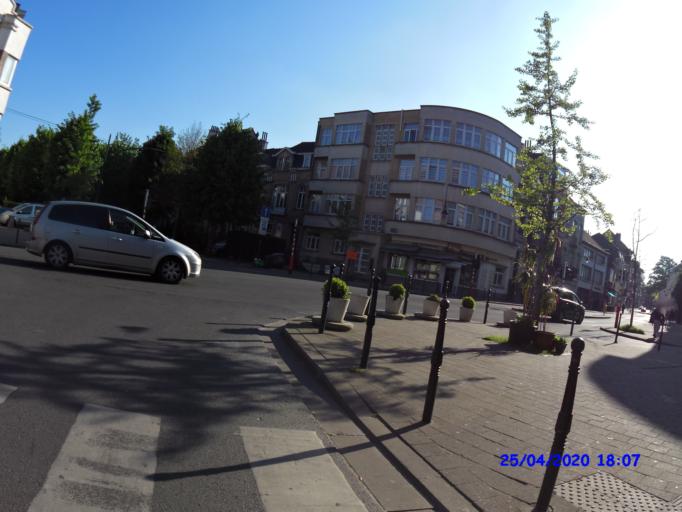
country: BE
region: Brussels Capital
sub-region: Bruxelles-Capitale
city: Brussels
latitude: 50.8771
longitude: 4.3418
